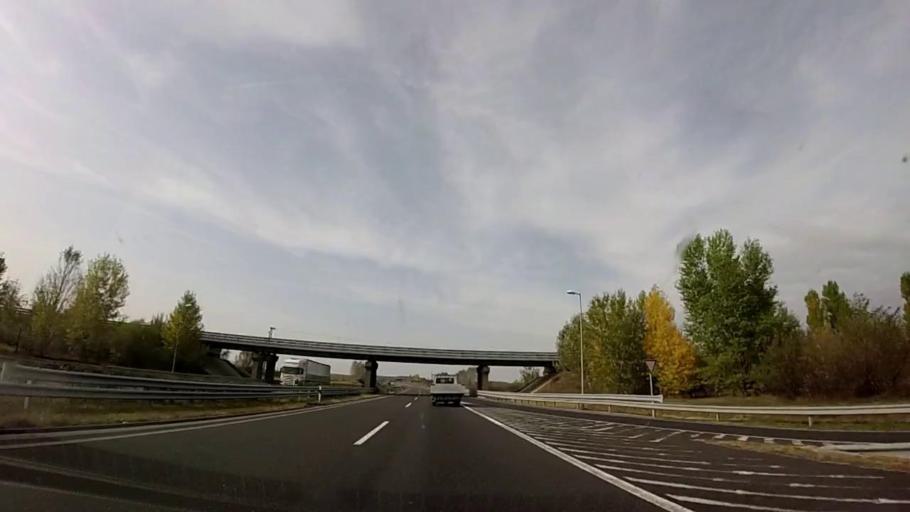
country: HU
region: Somogy
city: Kethely
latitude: 46.6839
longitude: 17.3765
